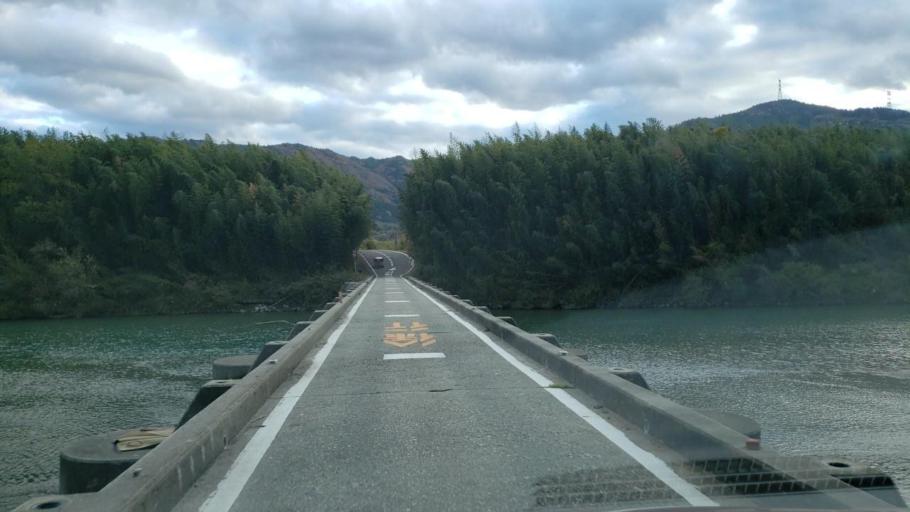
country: JP
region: Tokushima
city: Wakimachi
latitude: 34.0647
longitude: 134.1432
